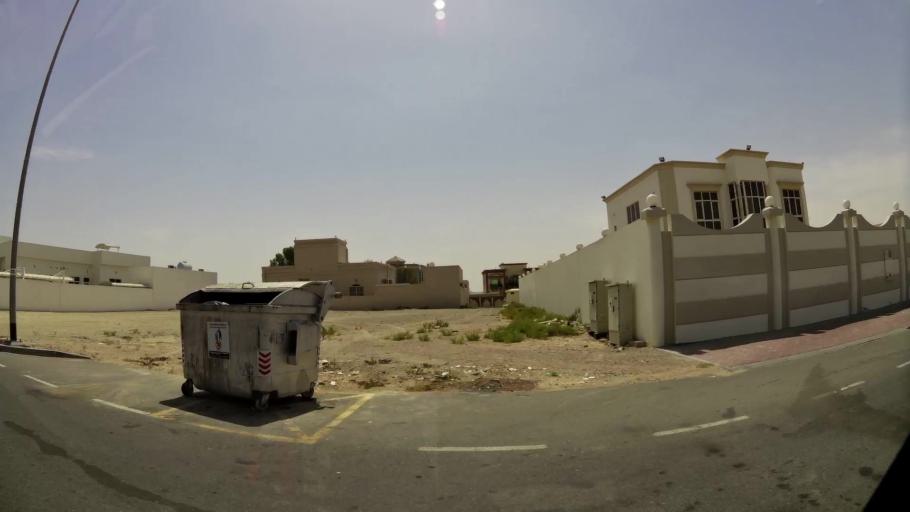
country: AE
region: Ash Shariqah
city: Sharjah
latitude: 25.1852
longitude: 55.4130
